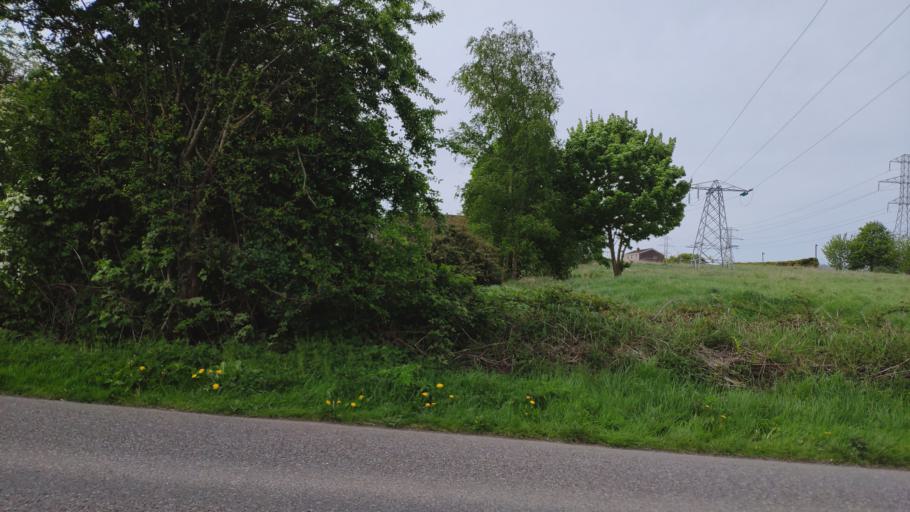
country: IE
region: Munster
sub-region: County Cork
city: Cork
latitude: 51.9225
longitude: -8.4559
